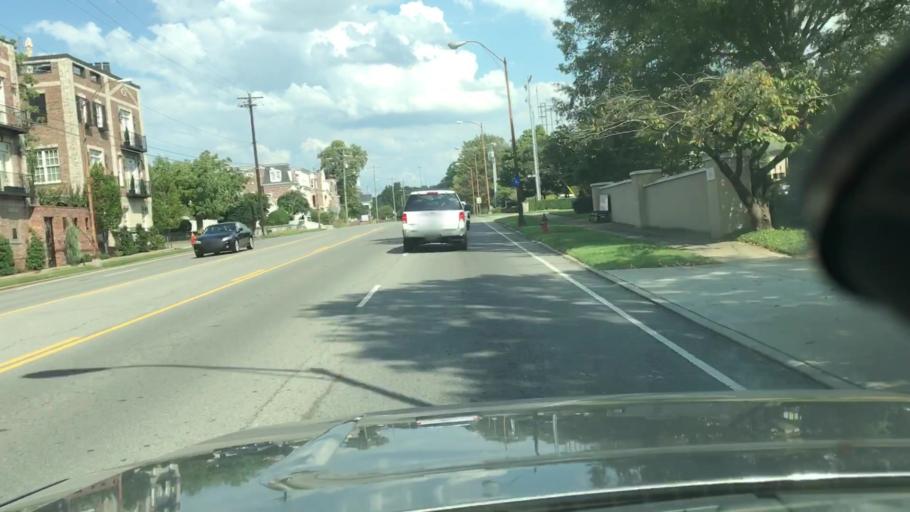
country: US
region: Tennessee
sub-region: Davidson County
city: Belle Meade
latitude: 36.1334
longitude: -86.8283
